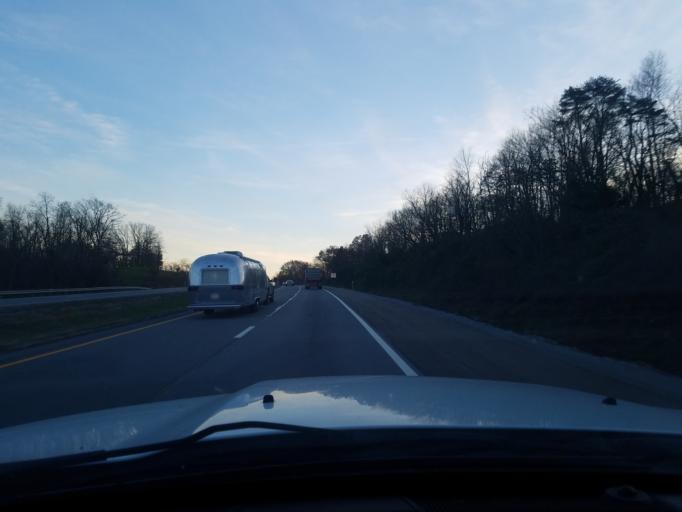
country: US
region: West Virginia
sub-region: Wood County
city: Williamstown
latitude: 39.3785
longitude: -81.4402
